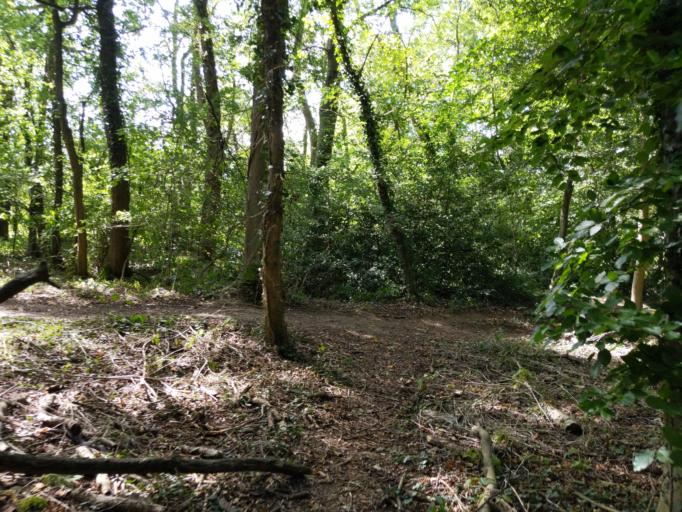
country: GB
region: England
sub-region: Oxfordshire
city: Radley
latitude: 51.7014
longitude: -1.2471
